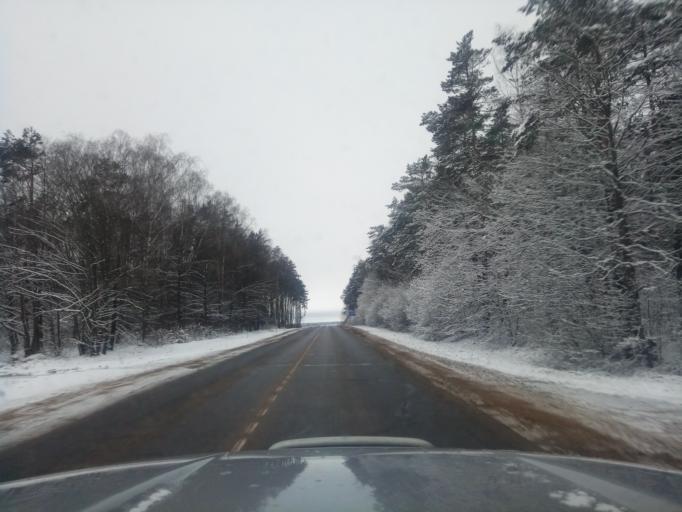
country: BY
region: Minsk
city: Kapyl'
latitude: 53.1562
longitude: 27.1090
